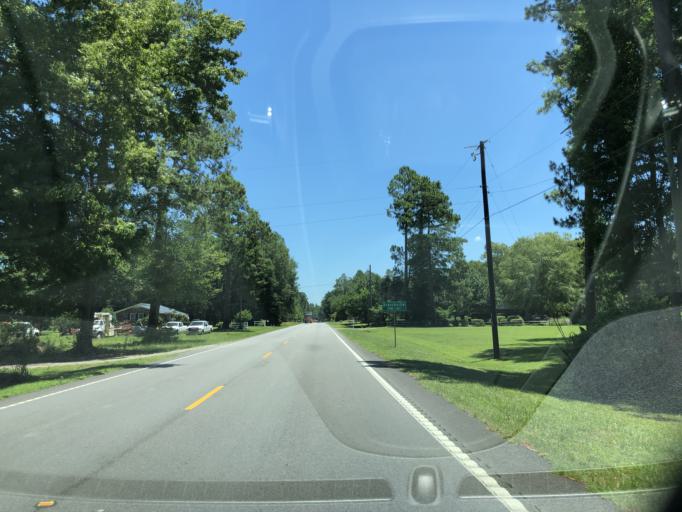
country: US
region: South Carolina
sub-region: Orangeburg County
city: Branchville
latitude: 33.2488
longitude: -80.8335
